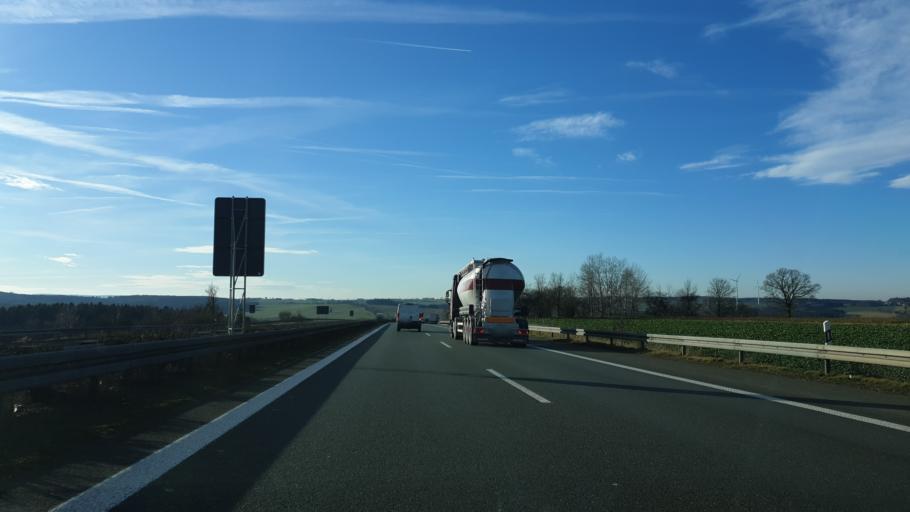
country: DE
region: Saxony
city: Reichenbach/Vogtland
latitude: 50.5899
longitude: 12.3269
